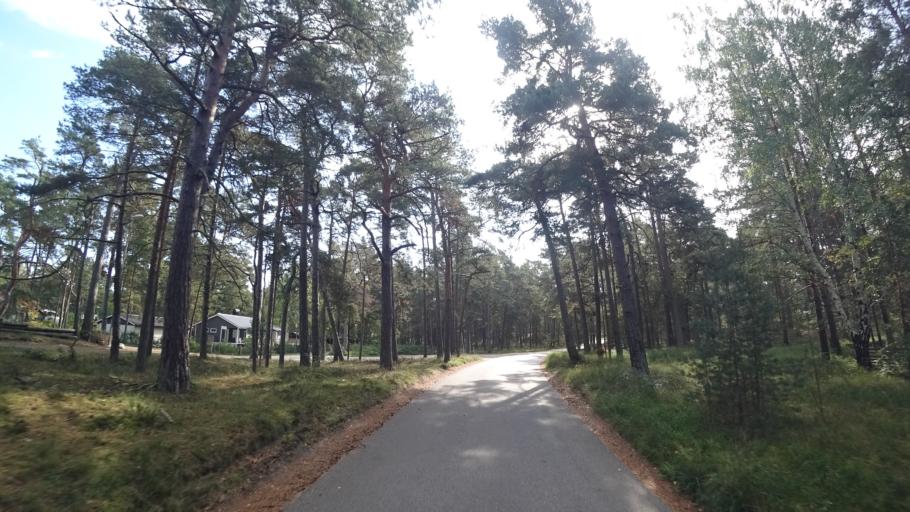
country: SE
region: Skane
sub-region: Kristianstads Kommun
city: Ahus
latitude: 55.9169
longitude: 14.2986
